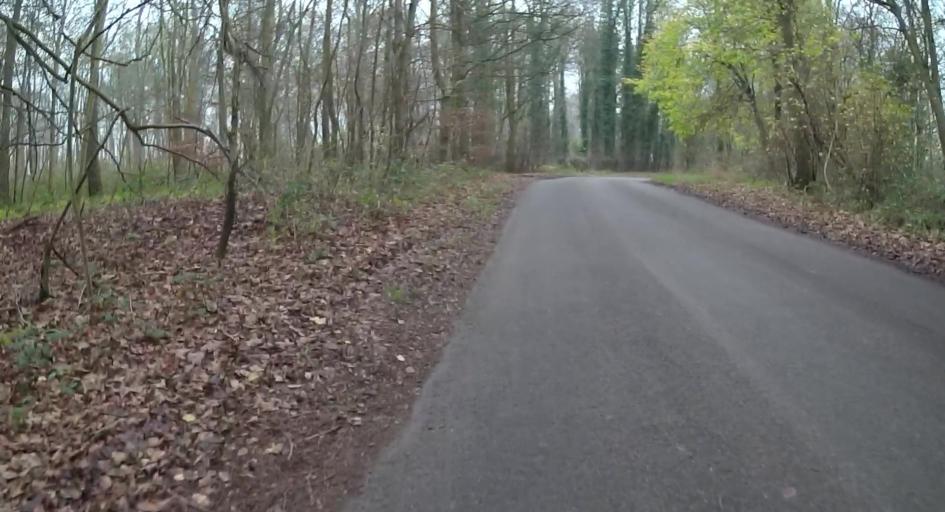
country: GB
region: England
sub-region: Hampshire
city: Kings Worthy
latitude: 51.1310
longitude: -1.2110
